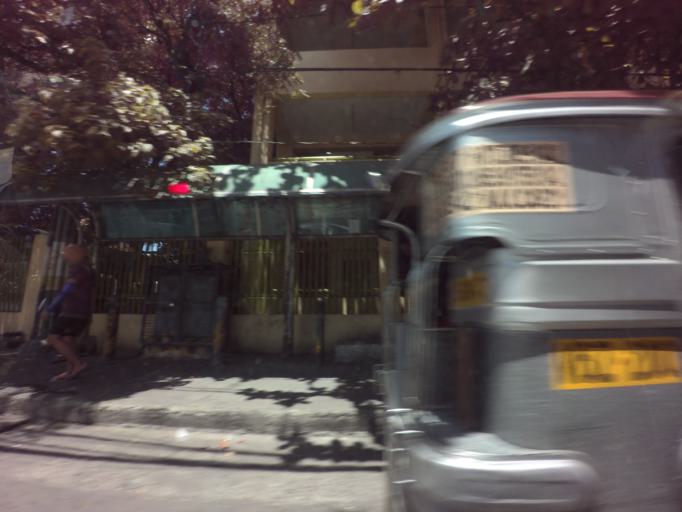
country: PH
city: Sambayanihan People's Village
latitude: 14.4913
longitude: 120.9894
